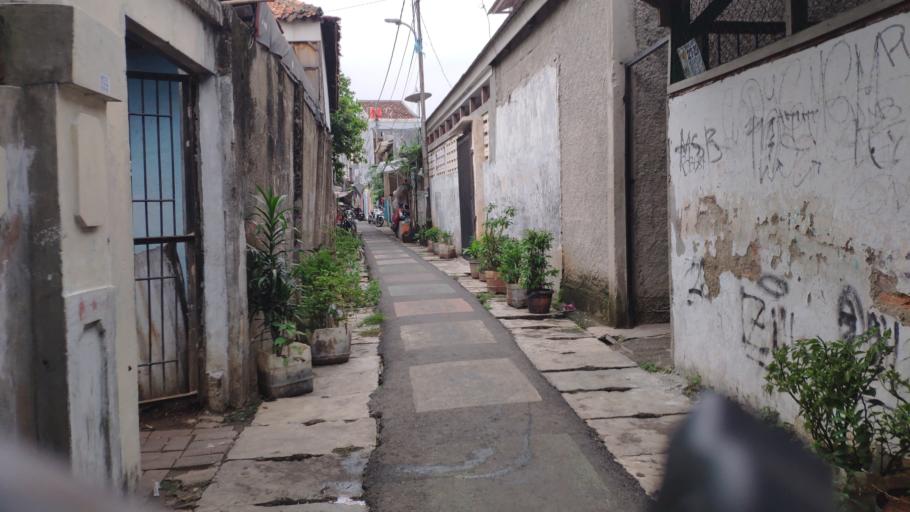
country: ID
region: Jakarta Raya
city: Jakarta
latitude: -6.2145
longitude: 106.8393
